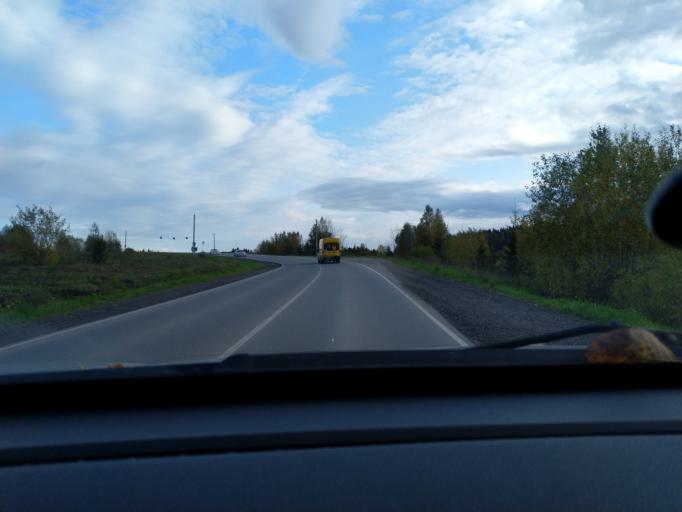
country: RU
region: Perm
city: Polazna
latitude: 58.2760
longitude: 56.4149
